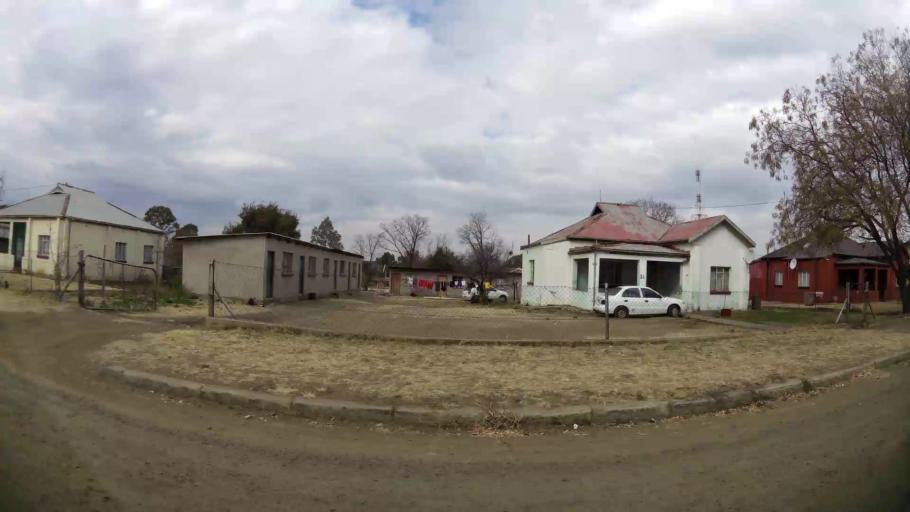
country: ZA
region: Orange Free State
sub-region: Fezile Dabi District Municipality
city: Kroonstad
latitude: -27.6565
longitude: 27.2345
